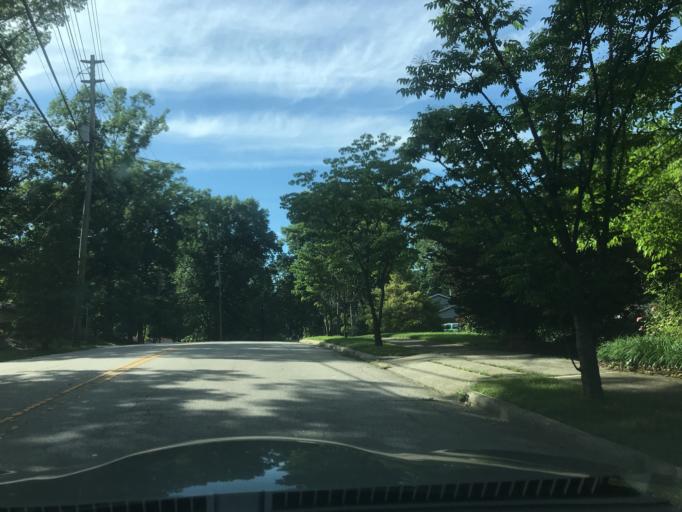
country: US
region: North Carolina
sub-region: Wake County
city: Raleigh
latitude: 35.8264
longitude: -78.6006
